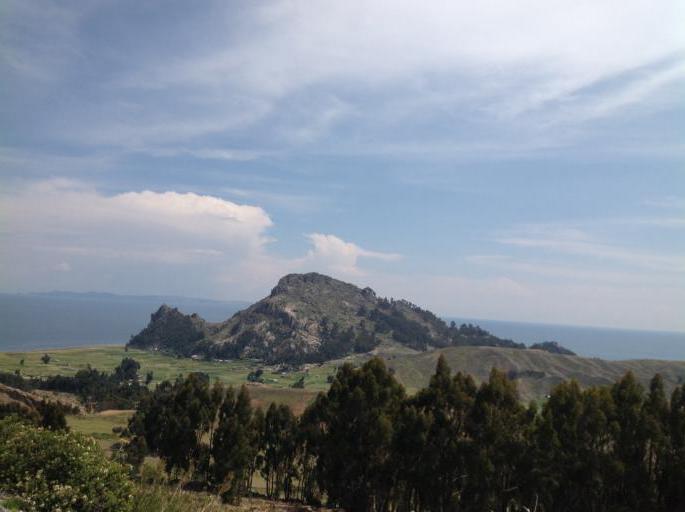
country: BO
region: La Paz
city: Yumani
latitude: -15.8513
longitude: -68.9887
